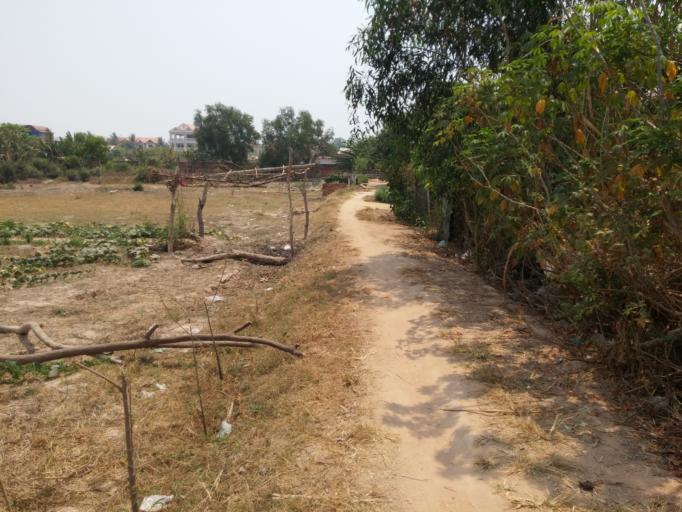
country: KH
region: Siem Reap
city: Siem Reap
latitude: 13.3599
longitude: 103.8918
